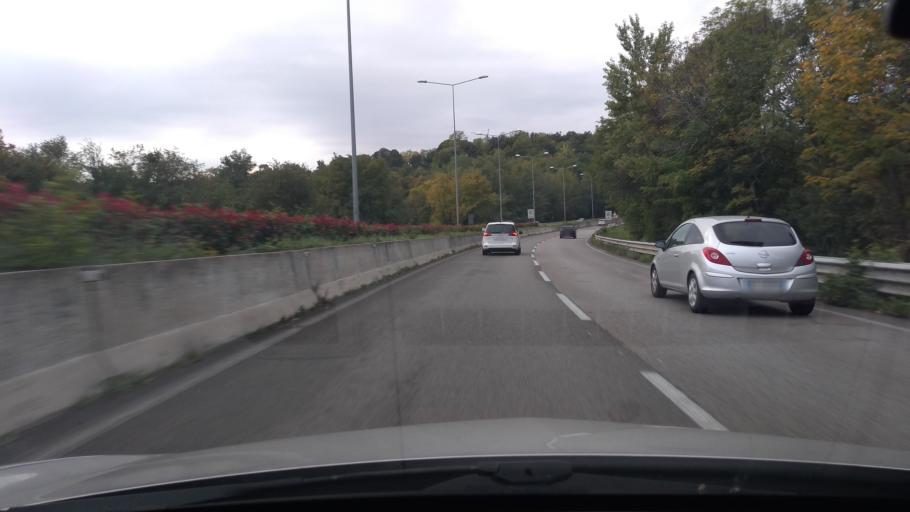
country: IT
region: Lombardy
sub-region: Provincia di Bergamo
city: Ghiaie
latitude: 45.6736
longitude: 9.5799
